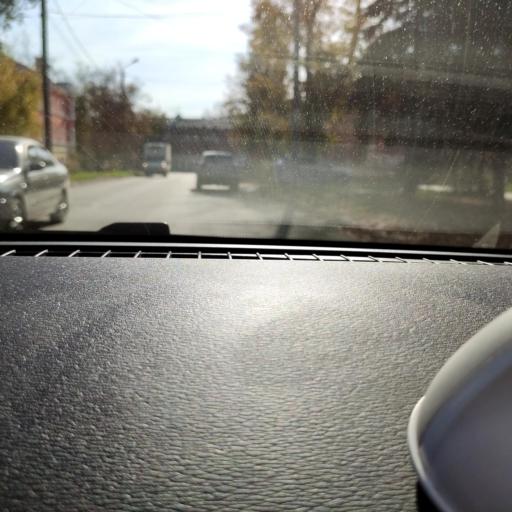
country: RU
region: Samara
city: Samara
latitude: 53.1988
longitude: 50.2191
